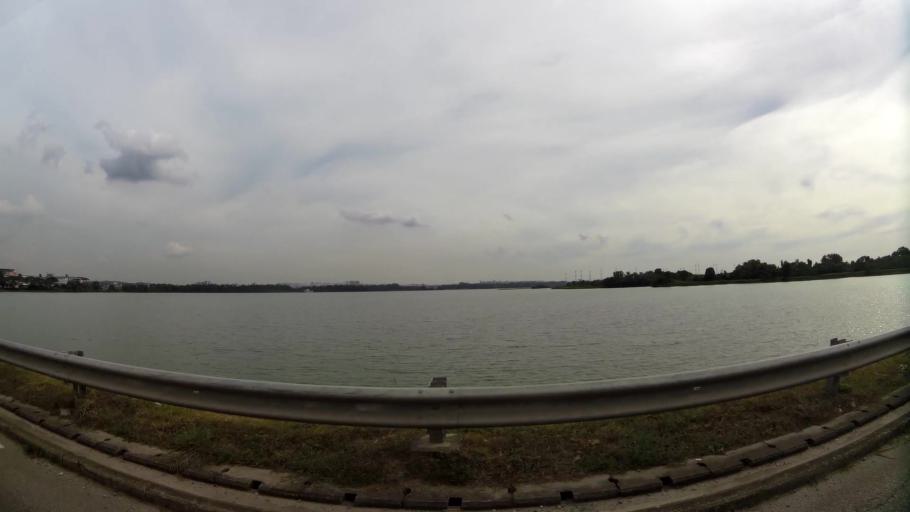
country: MY
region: Johor
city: Johor Bahru
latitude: 1.4386
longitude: 103.7393
